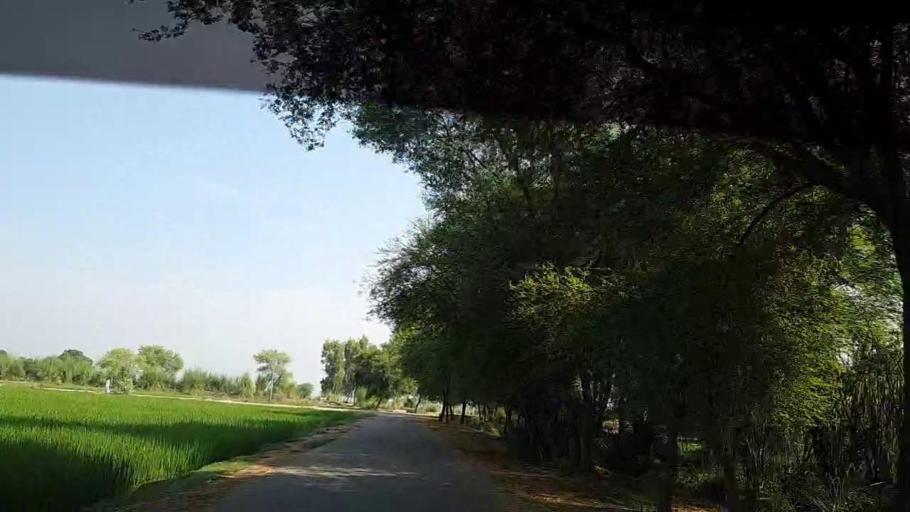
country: PK
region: Sindh
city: Shikarpur
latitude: 28.0920
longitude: 68.6774
